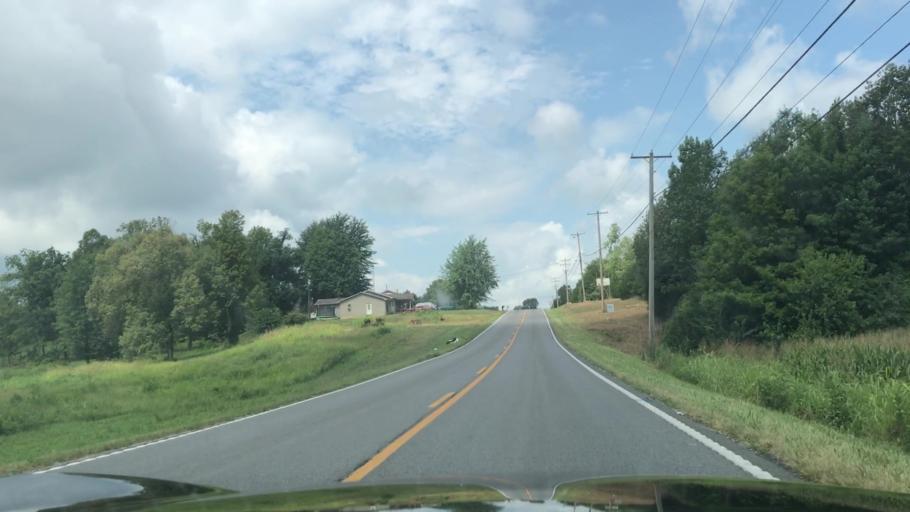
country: US
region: Kentucky
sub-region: Muhlenberg County
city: Greenville
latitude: 37.2056
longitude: -87.1513
